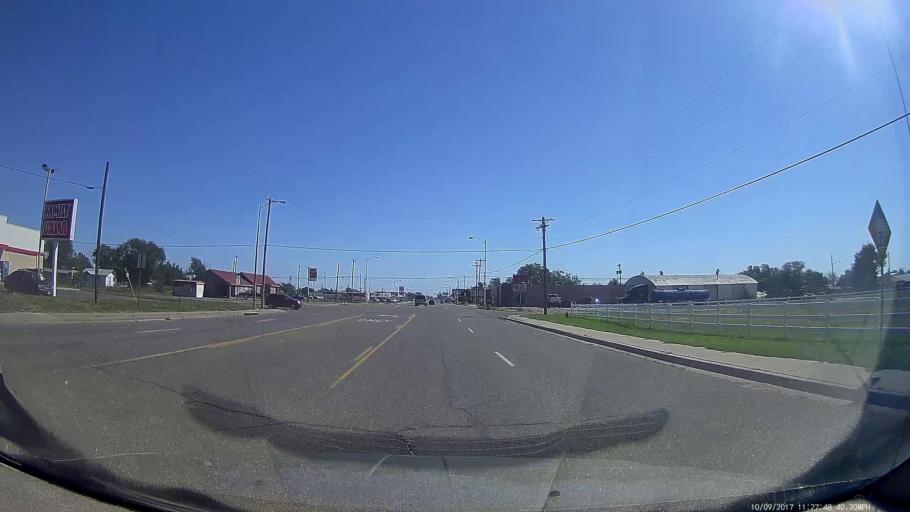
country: US
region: New Mexico
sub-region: Curry County
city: Clovis
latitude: 34.4047
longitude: -103.2229
